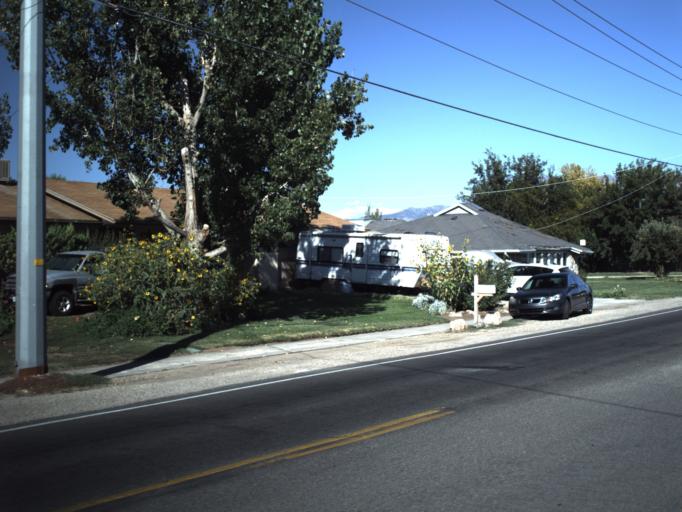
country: US
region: Utah
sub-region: Davis County
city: Clinton
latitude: 41.1398
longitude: -112.0738
